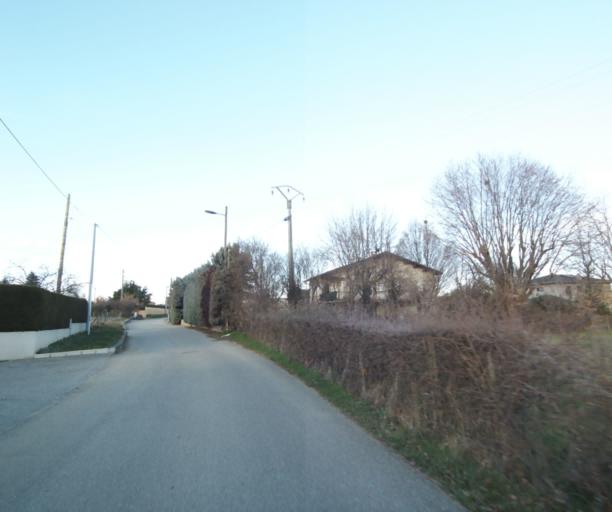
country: FR
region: Rhone-Alpes
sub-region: Departement de l'Ardeche
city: Davezieux
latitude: 45.2471
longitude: 4.6976
